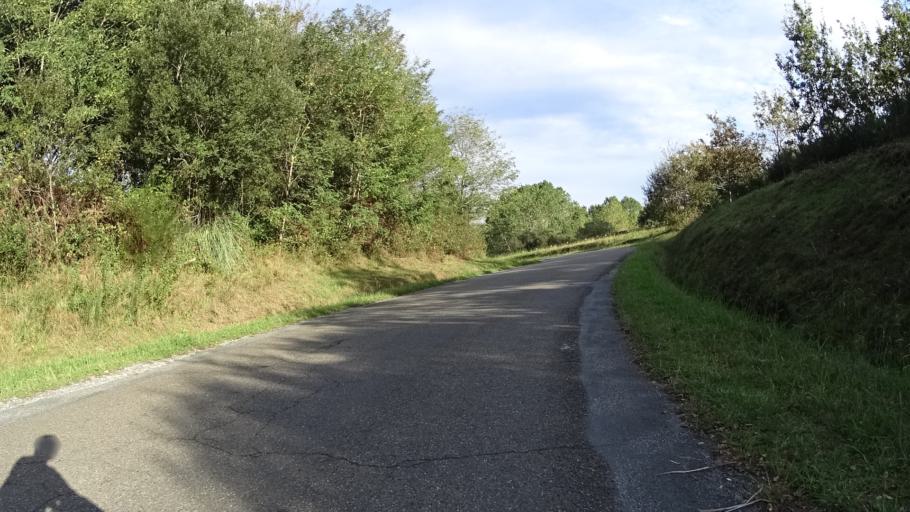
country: FR
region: Aquitaine
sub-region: Departement des Landes
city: Saint-Paul-les-Dax
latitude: 43.7420
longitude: -1.0729
